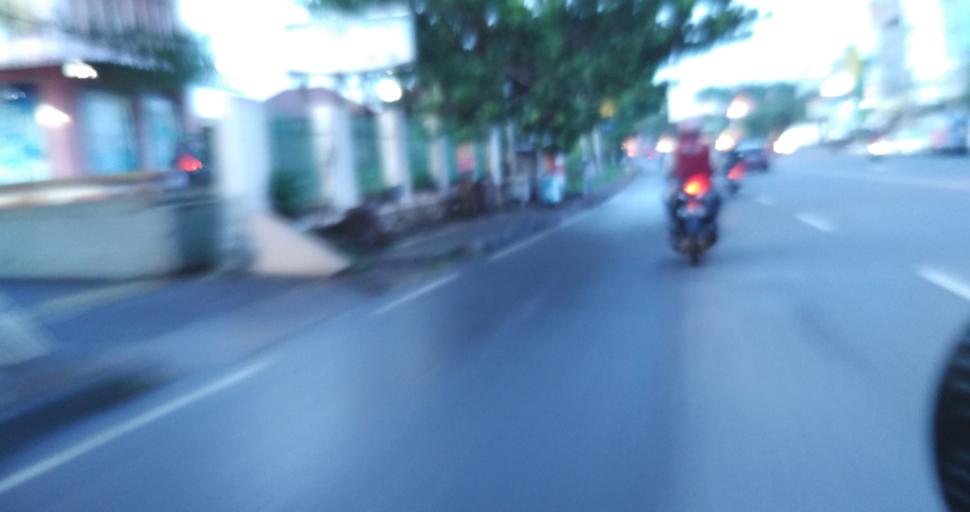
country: ID
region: Central Java
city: Semarang
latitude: -7.0511
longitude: 110.4178
